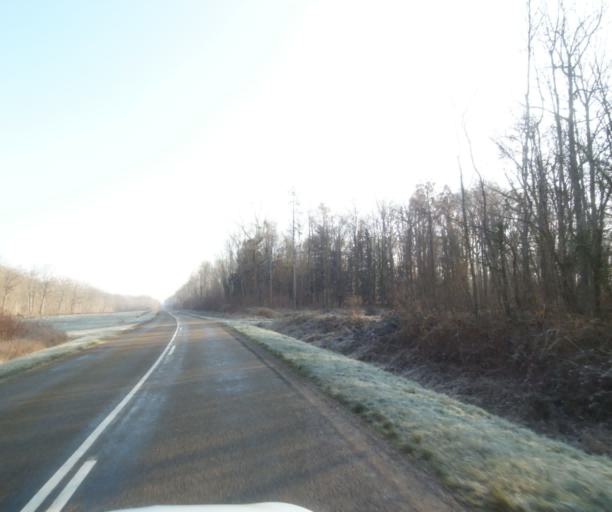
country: FR
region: Champagne-Ardenne
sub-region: Departement de la Haute-Marne
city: Laneuville-a-Remy
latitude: 48.4924
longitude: 4.8830
